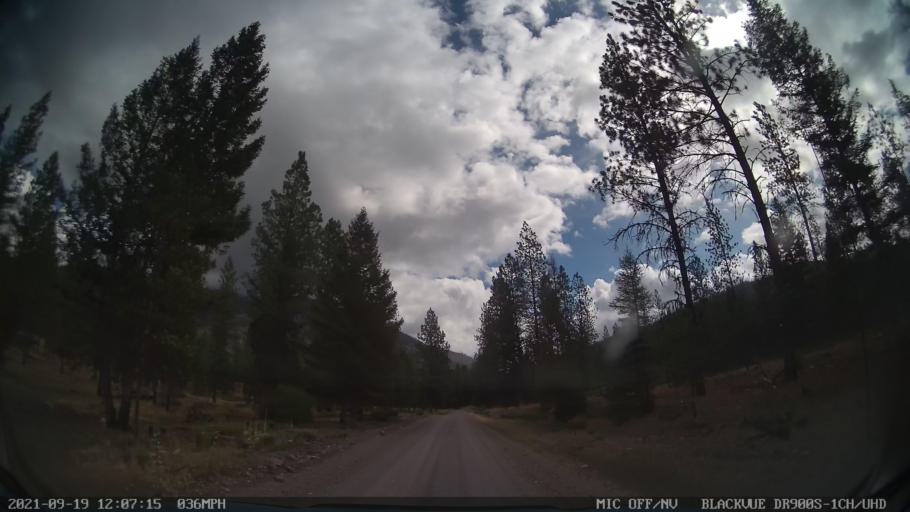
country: US
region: Montana
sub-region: Missoula County
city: Seeley Lake
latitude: 47.1843
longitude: -113.4093
